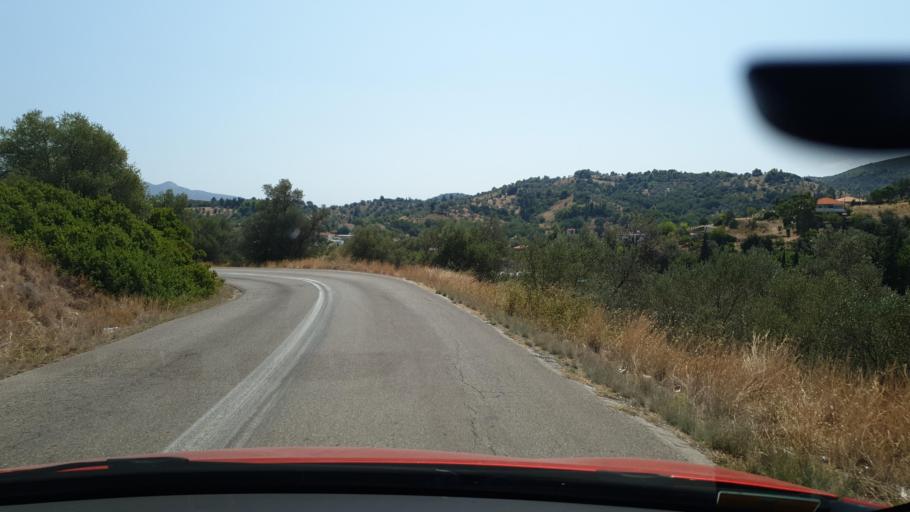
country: GR
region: Central Greece
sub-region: Nomos Evvoias
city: Oxilithos
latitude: 38.5313
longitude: 24.0856
